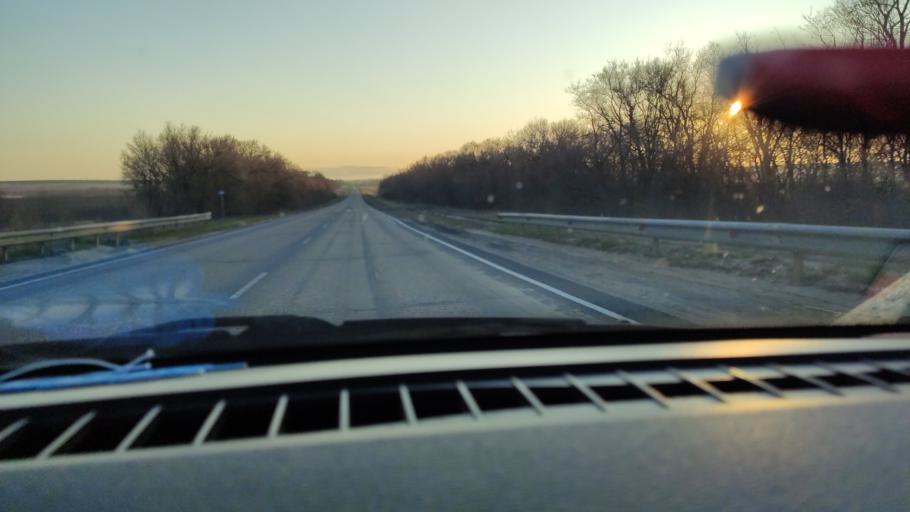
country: RU
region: Saratov
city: Sinodskoye
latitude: 51.9647
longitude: 46.6308
